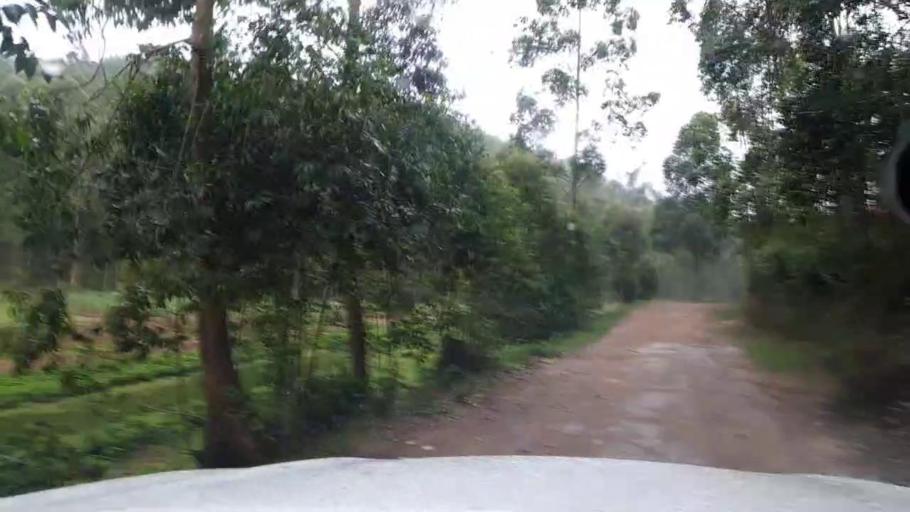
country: RW
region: Northern Province
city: Byumba
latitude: -1.6530
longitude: 29.9248
